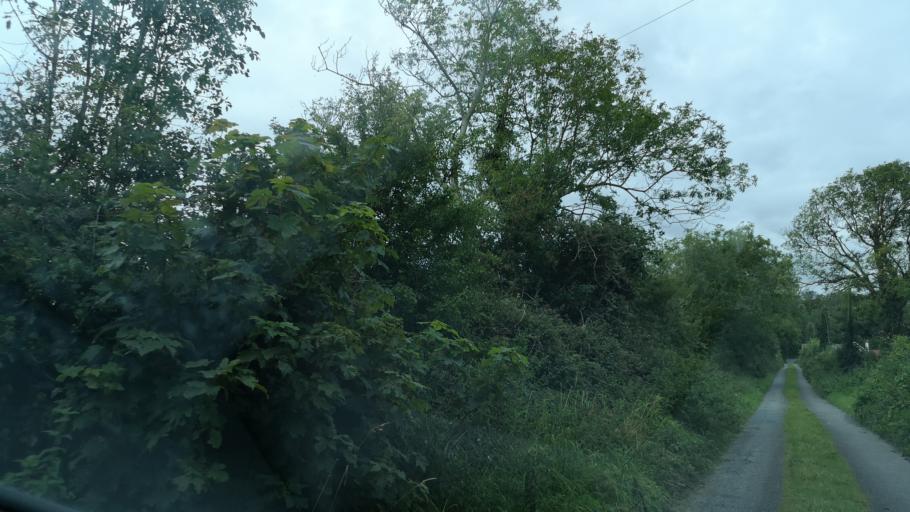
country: IE
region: Connaught
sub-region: County Galway
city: Loughrea
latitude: 53.1566
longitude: -8.4401
